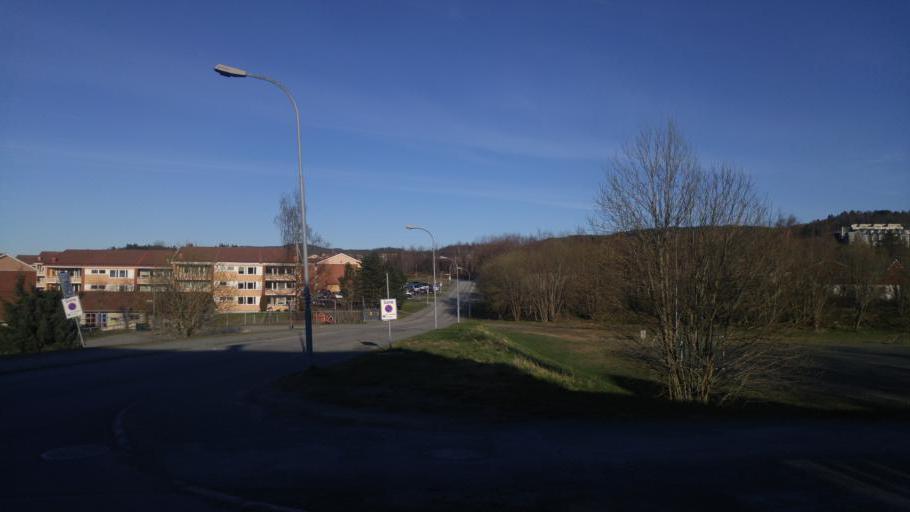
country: NO
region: Sor-Trondelag
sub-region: Trondheim
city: Trondheim
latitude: 63.4154
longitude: 10.4457
